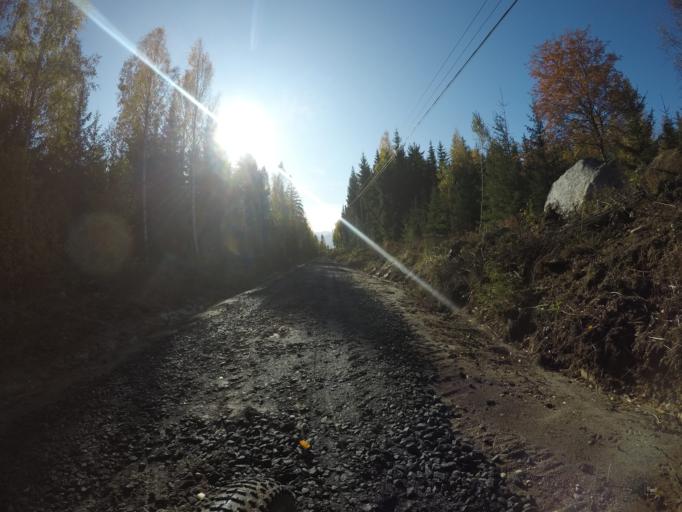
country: SE
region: Vaestmanland
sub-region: Kungsors Kommun
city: Kungsoer
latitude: 59.3137
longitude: 16.0979
